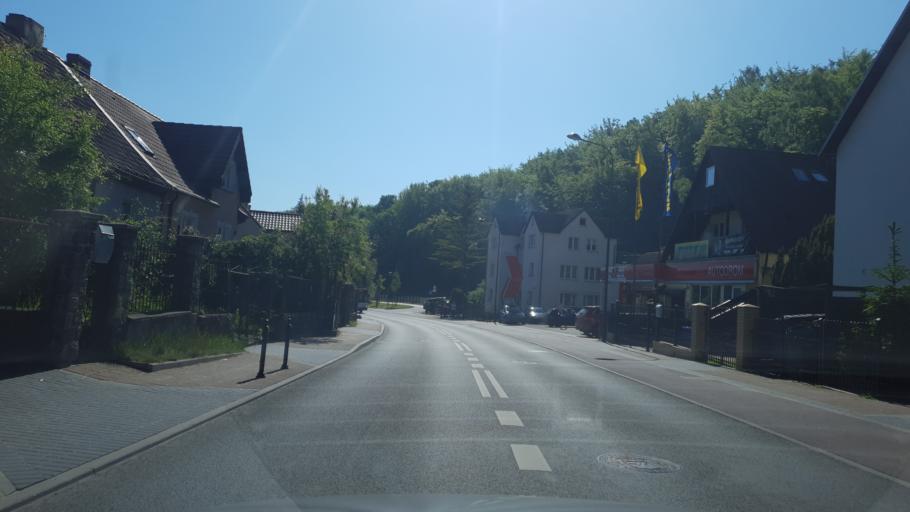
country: PL
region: Pomeranian Voivodeship
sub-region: Sopot
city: Sopot
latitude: 54.4554
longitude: 18.5444
